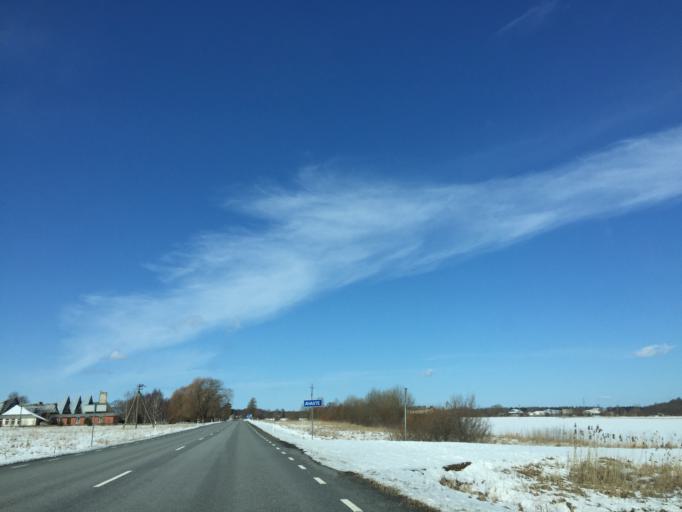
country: EE
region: Paernumaa
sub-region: Audru vald
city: Audru
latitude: 58.4685
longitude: 24.2025
